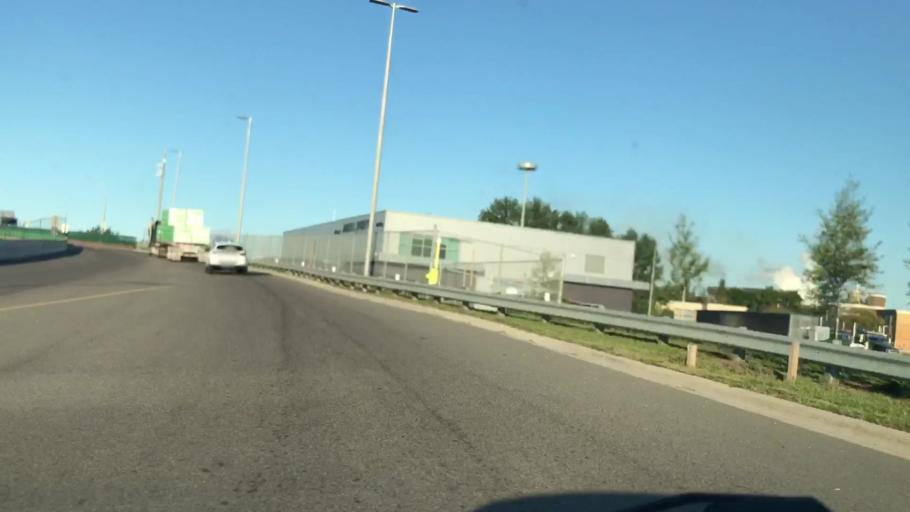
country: CA
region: Ontario
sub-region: Algoma
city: Sault Ste. Marie
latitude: 46.5194
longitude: -84.3516
